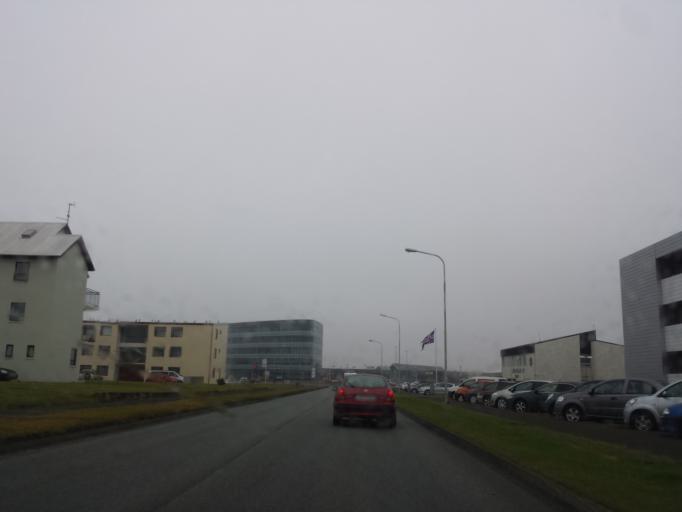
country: IS
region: Southern Peninsula
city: Reykjanesbaer
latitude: 63.9965
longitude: -22.5538
